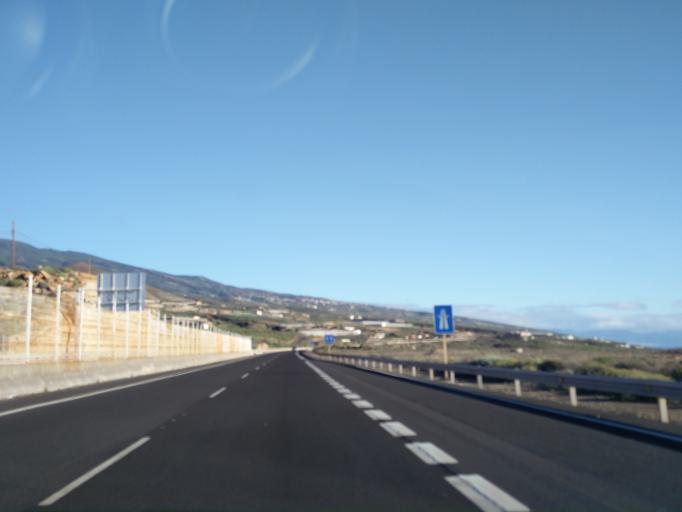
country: ES
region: Canary Islands
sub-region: Provincia de Santa Cruz de Tenerife
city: Fasnia
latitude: 28.2028
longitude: -16.4262
